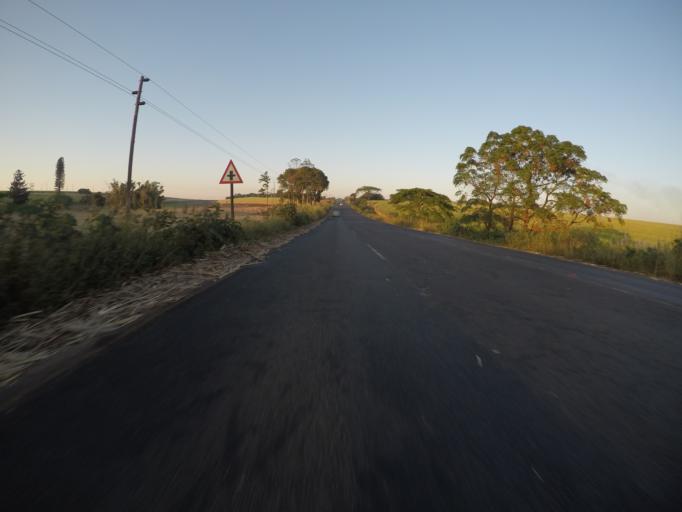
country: ZA
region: KwaZulu-Natal
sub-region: uThungulu District Municipality
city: Empangeni
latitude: -28.7868
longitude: 31.8975
